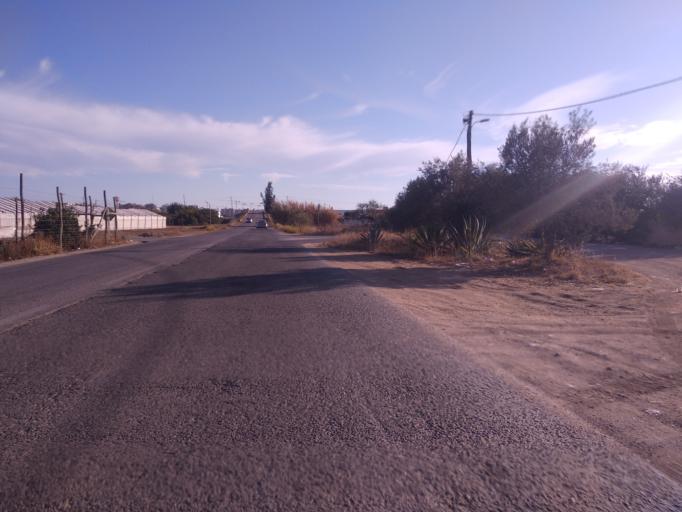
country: PT
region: Faro
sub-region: Faro
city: Faro
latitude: 37.0449
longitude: -7.9379
